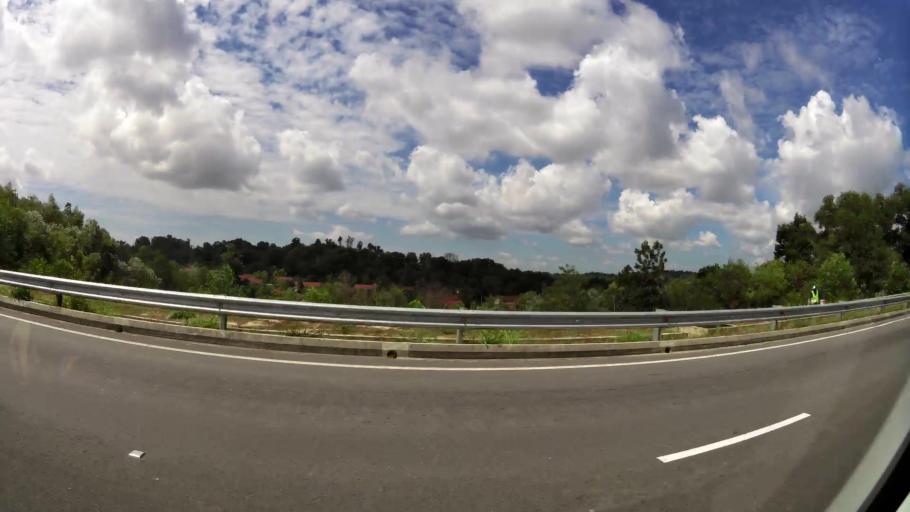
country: BN
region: Brunei and Muara
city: Bandar Seri Begawan
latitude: 4.9323
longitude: 114.8899
